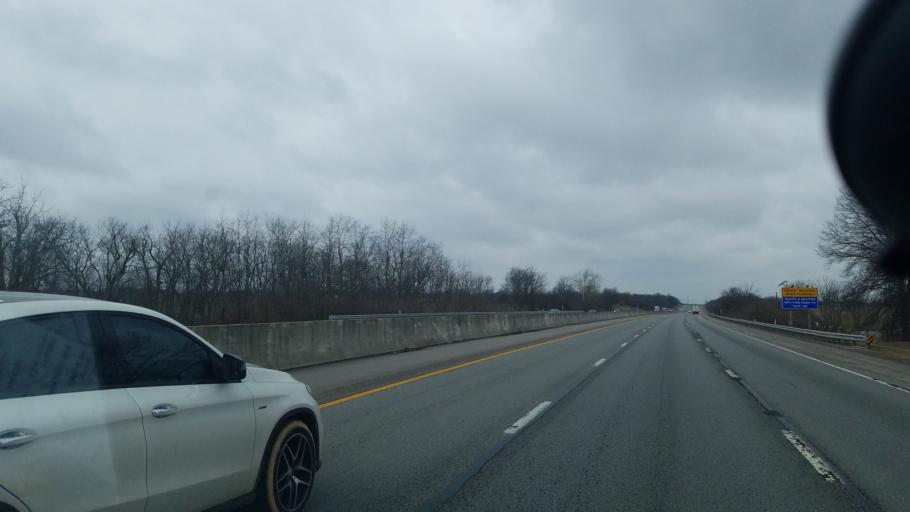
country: US
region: Kentucky
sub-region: Clark County
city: Winchester
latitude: 38.0378
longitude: -84.2932
